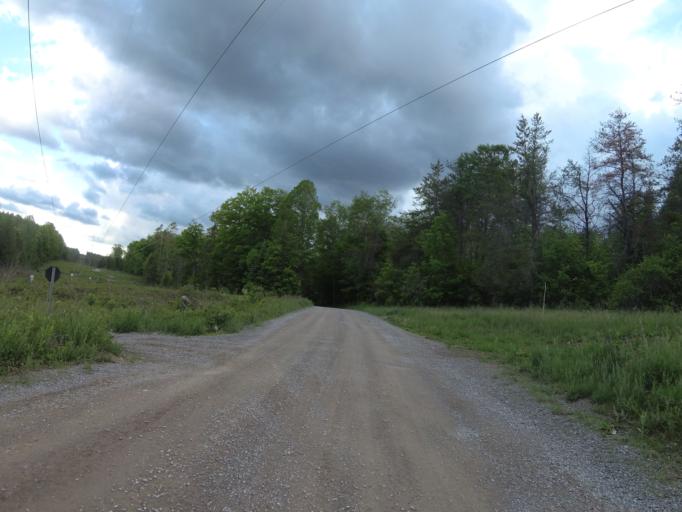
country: CA
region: Ontario
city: Renfrew
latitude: 45.1897
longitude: -76.9015
